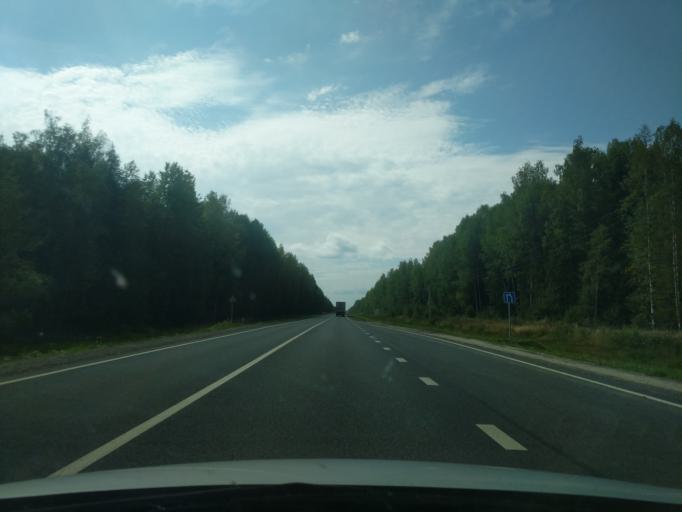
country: RU
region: Kostroma
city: Kadyy
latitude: 57.8146
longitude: 43.2313
